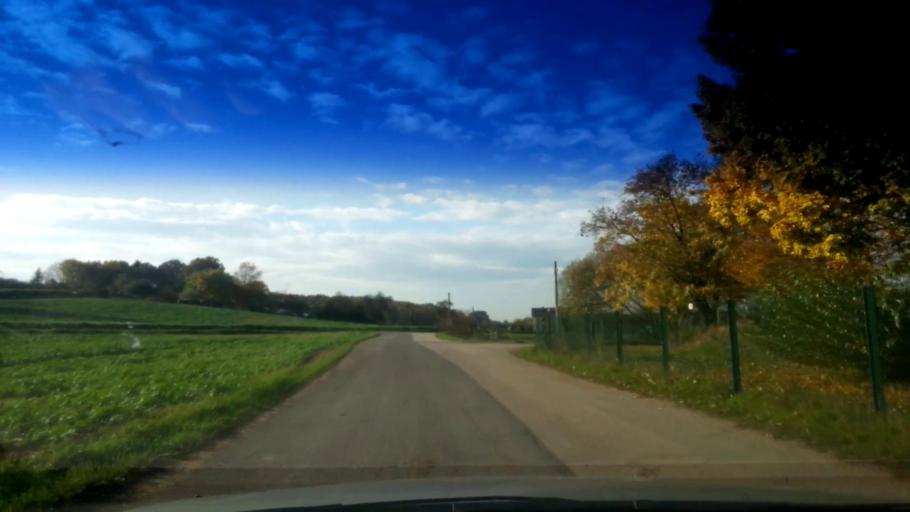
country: DE
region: Bavaria
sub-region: Upper Franconia
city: Stegaurach
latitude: 49.8513
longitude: 10.8676
